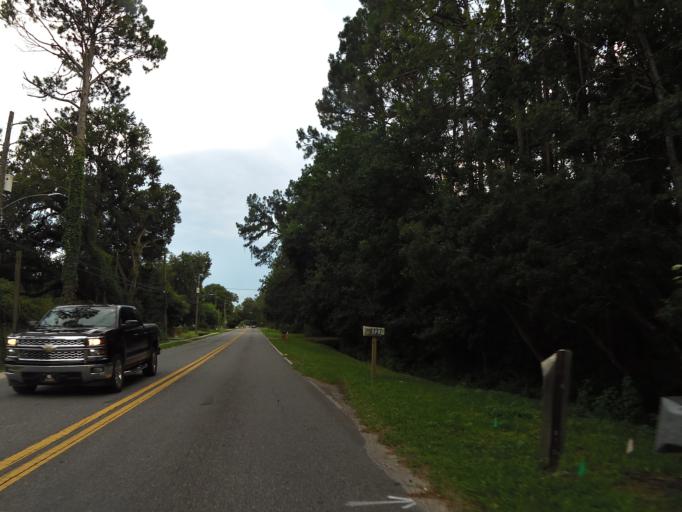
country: US
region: Florida
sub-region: Duval County
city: Jacksonville
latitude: 30.3327
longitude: -81.7898
